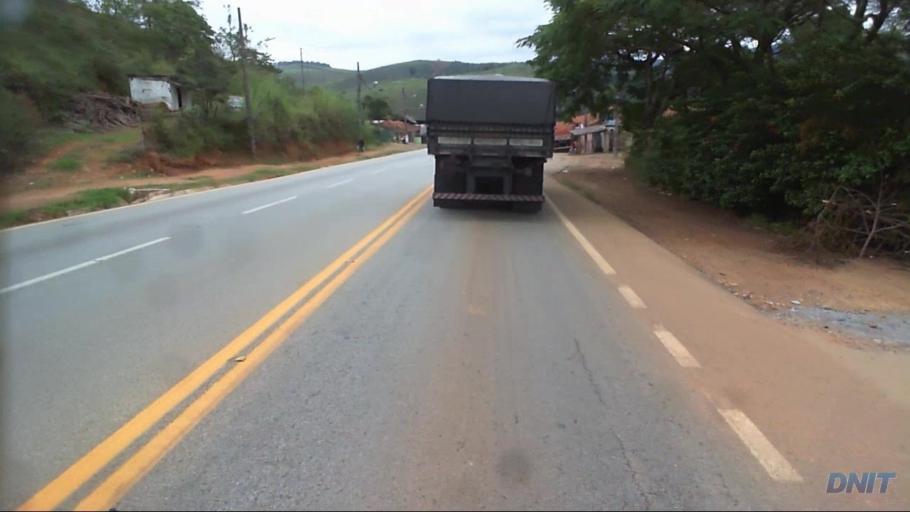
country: BR
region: Minas Gerais
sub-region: Nova Era
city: Nova Era
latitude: -19.8173
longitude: -43.0669
